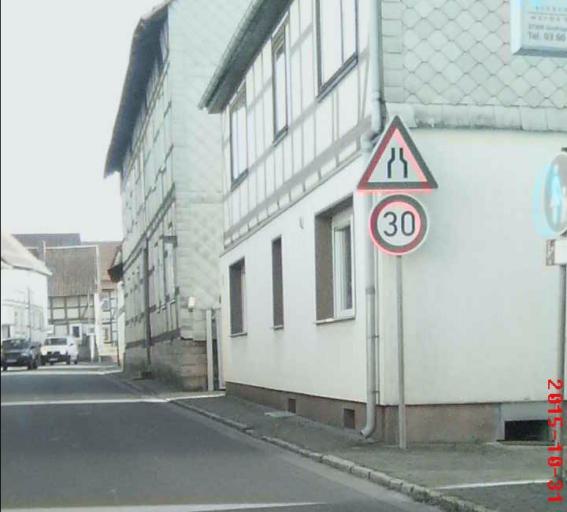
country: DE
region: Thuringia
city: Geismar
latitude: 51.2312
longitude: 10.1664
